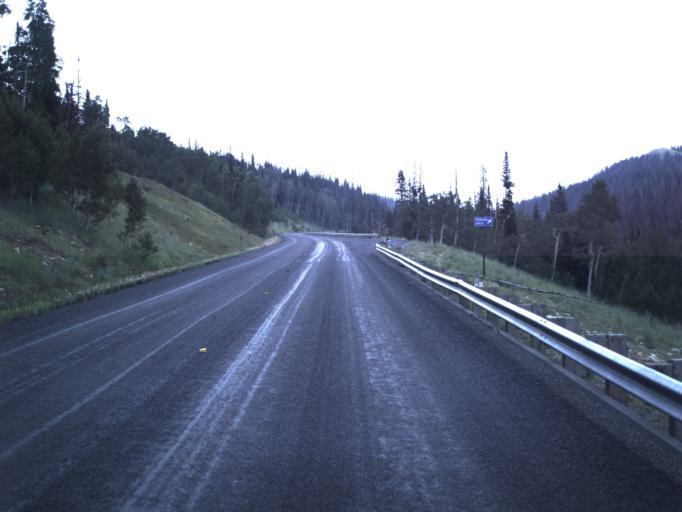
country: US
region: Utah
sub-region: Summit County
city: Francis
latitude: 40.5028
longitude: -111.0432
